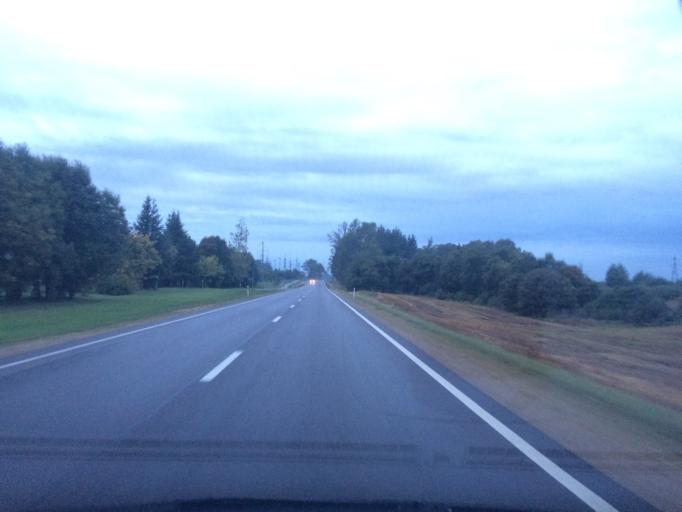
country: LV
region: Jekabpils Rajons
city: Jekabpils
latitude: 56.5258
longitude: 25.9770
